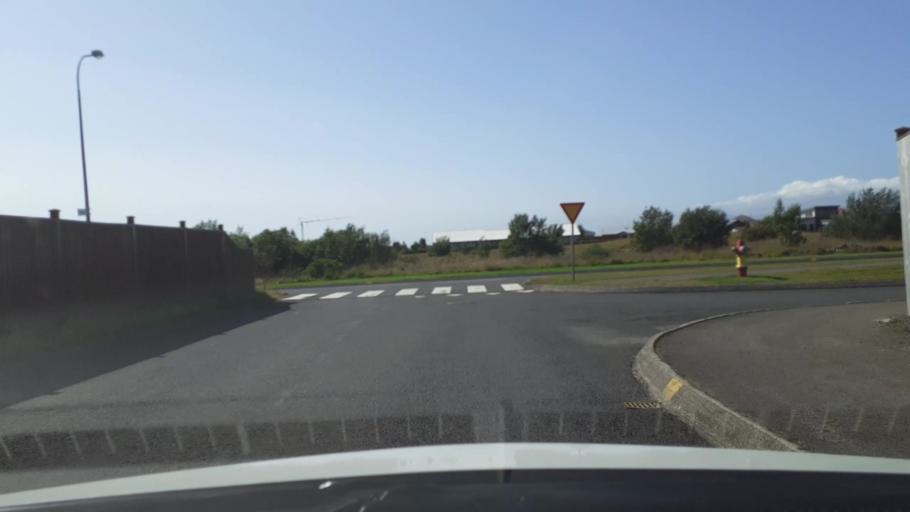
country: IS
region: South
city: Selfoss
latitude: 63.9333
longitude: -21.0194
